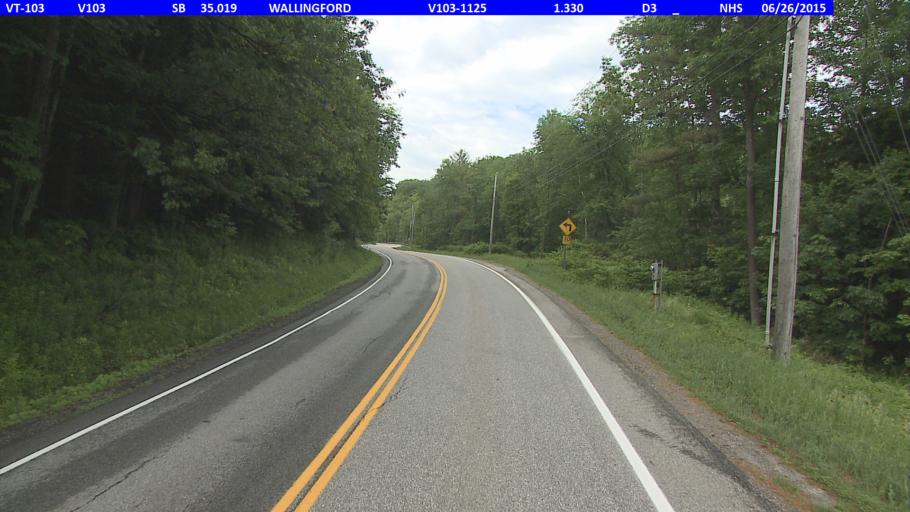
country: US
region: Vermont
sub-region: Rutland County
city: Rutland
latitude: 43.4690
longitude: -72.8747
